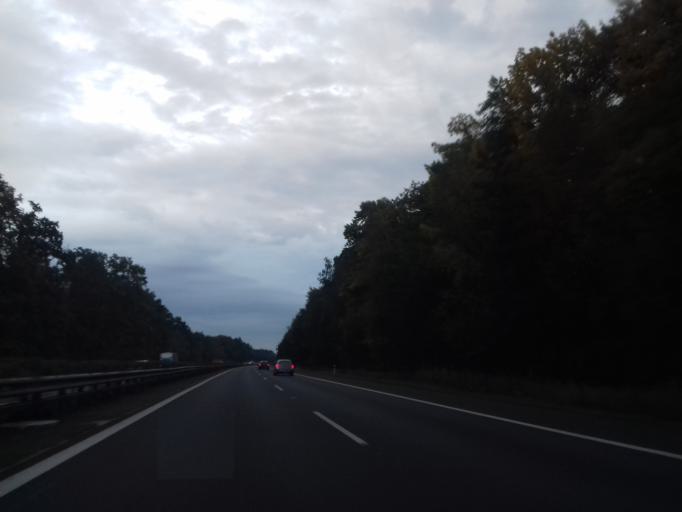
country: CZ
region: Central Bohemia
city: Poricany
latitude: 50.1253
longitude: 14.9200
